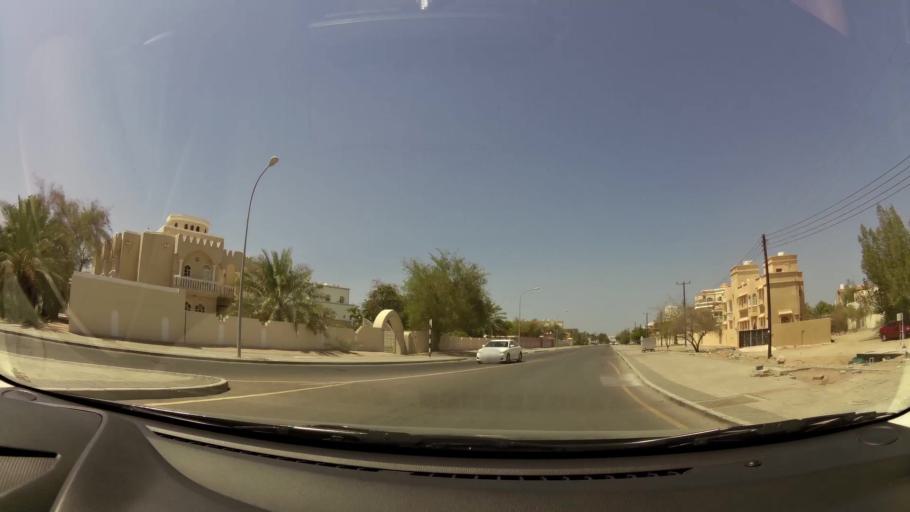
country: OM
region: Muhafazat Masqat
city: As Sib al Jadidah
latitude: 23.6258
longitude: 58.2221
